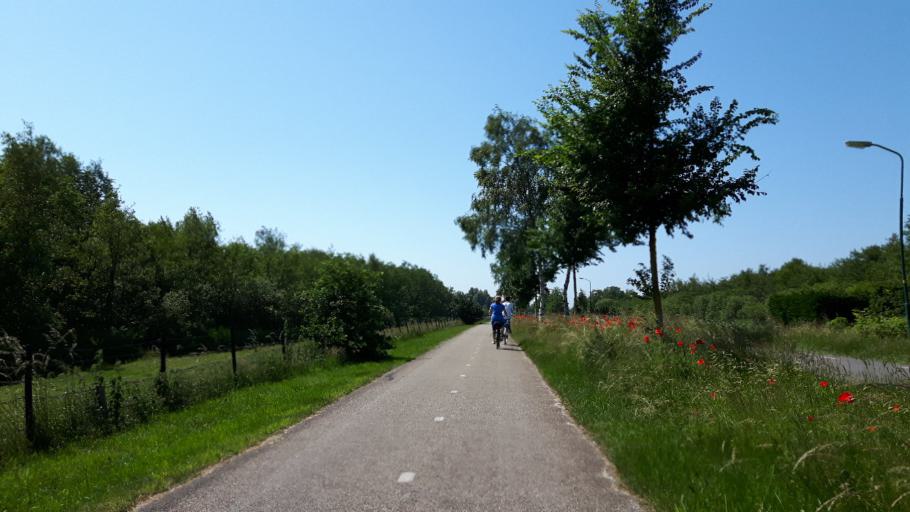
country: NL
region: North Holland
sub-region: Gemeente Wijdemeren
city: Kortenhoef
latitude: 52.2529
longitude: 5.1034
